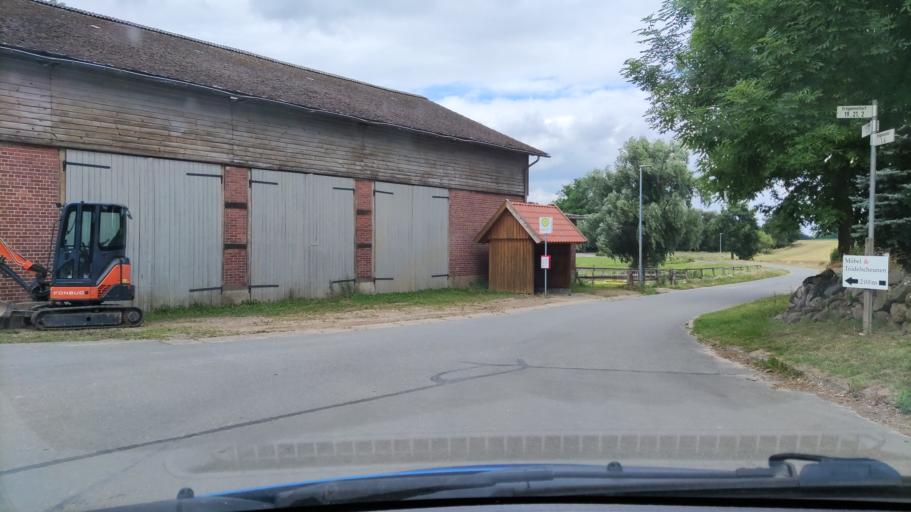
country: DE
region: Lower Saxony
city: Romstedt
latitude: 53.1033
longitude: 10.6545
